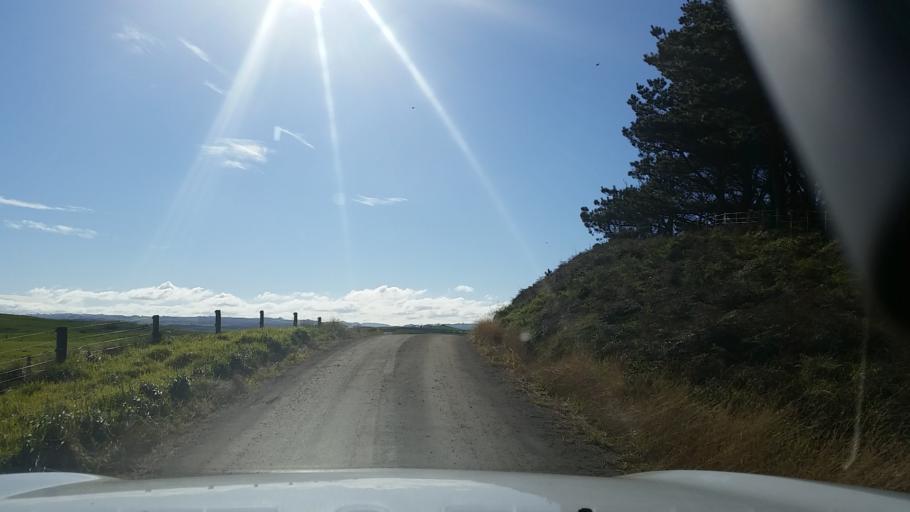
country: NZ
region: Taranaki
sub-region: South Taranaki District
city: Patea
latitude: -39.7815
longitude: 174.5467
